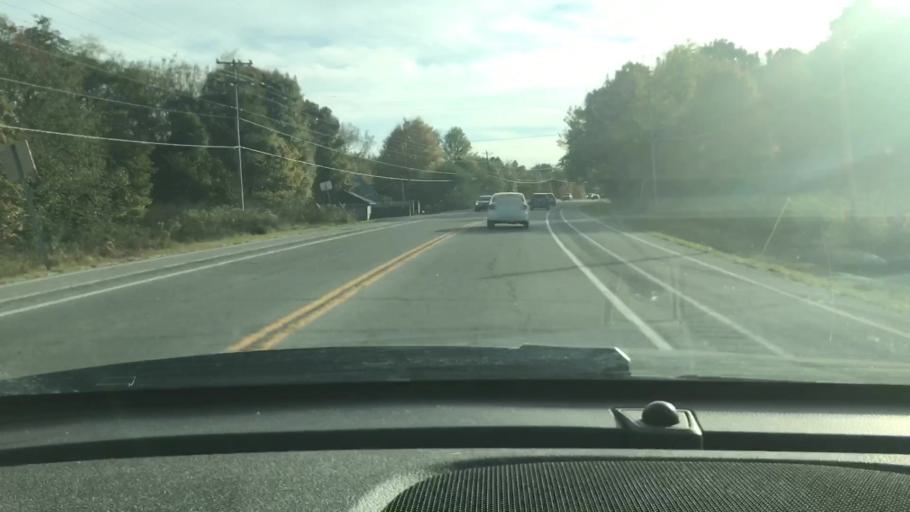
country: US
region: Tennessee
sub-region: Sumner County
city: White House
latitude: 36.4392
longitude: -86.6804
